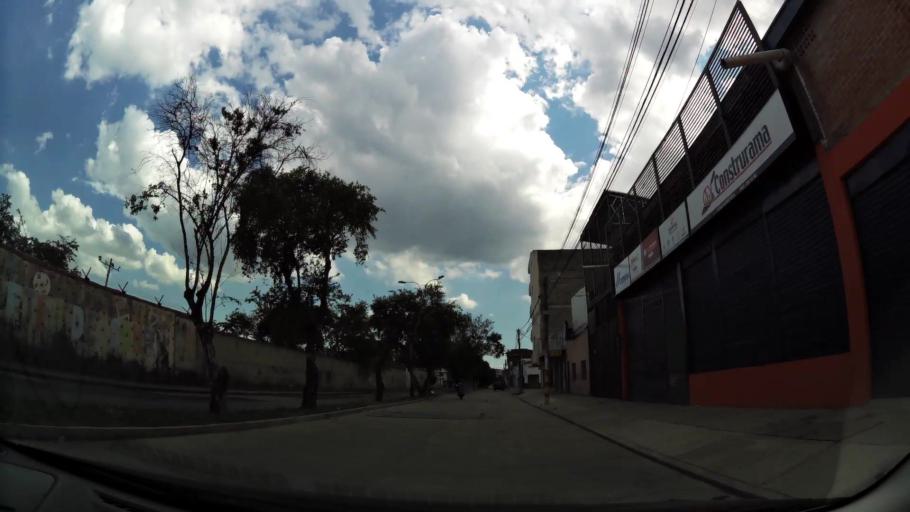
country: CO
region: Valle del Cauca
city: Cali
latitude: 3.4408
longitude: -76.5308
